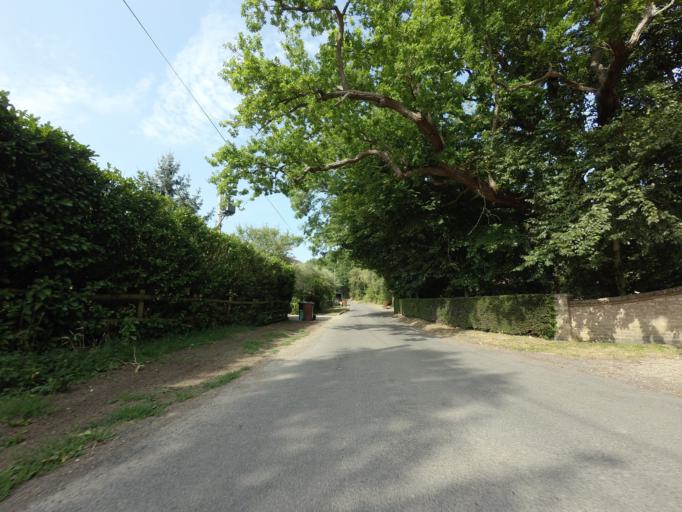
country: GB
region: England
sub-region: Kent
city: Headcorn
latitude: 51.1218
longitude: 0.5959
